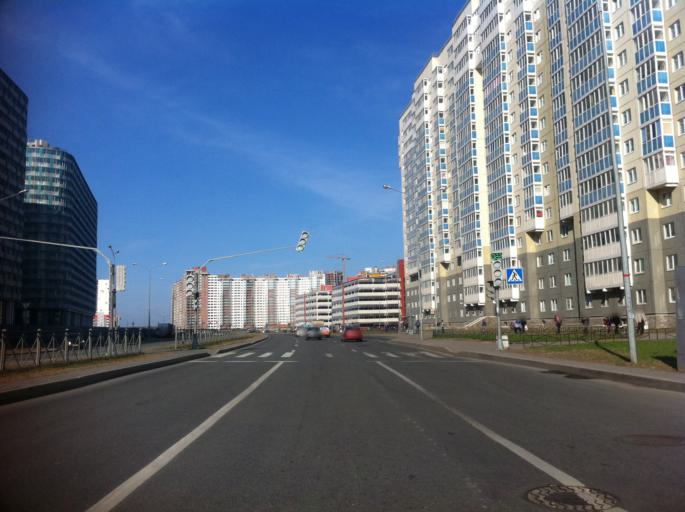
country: RU
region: St.-Petersburg
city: Uritsk
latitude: 59.8607
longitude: 30.1604
